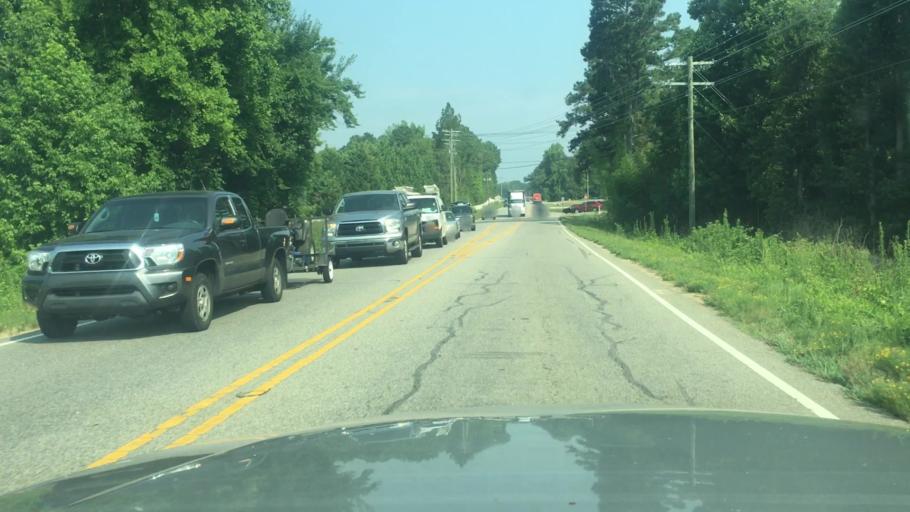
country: US
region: North Carolina
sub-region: Cumberland County
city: Hope Mills
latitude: 34.9288
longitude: -78.9133
